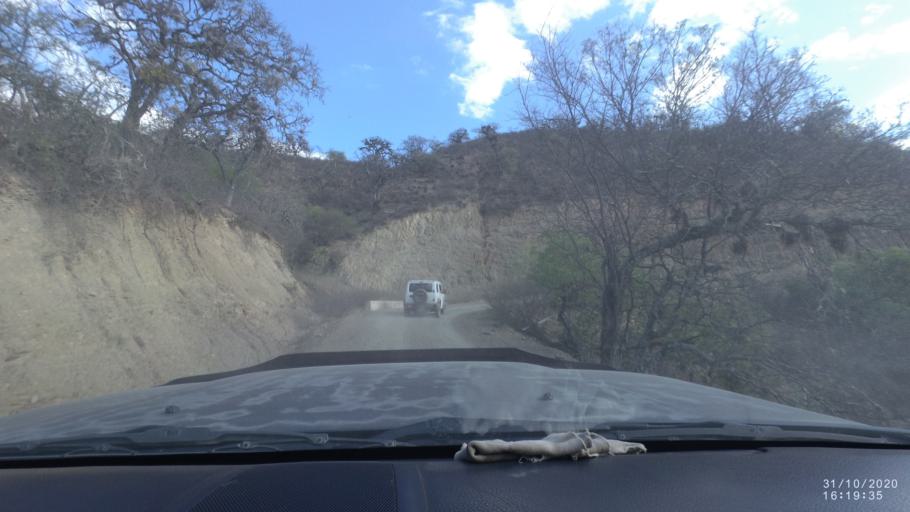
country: BO
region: Chuquisaca
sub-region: Provincia Zudanez
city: Mojocoya
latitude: -18.3963
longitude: -64.6023
